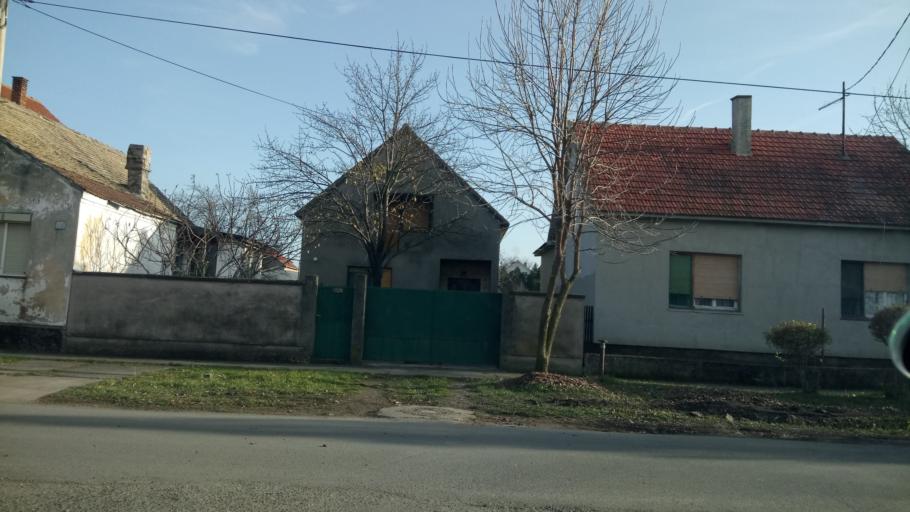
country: RS
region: Autonomna Pokrajina Vojvodina
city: Nova Pazova
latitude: 44.9471
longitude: 20.2322
